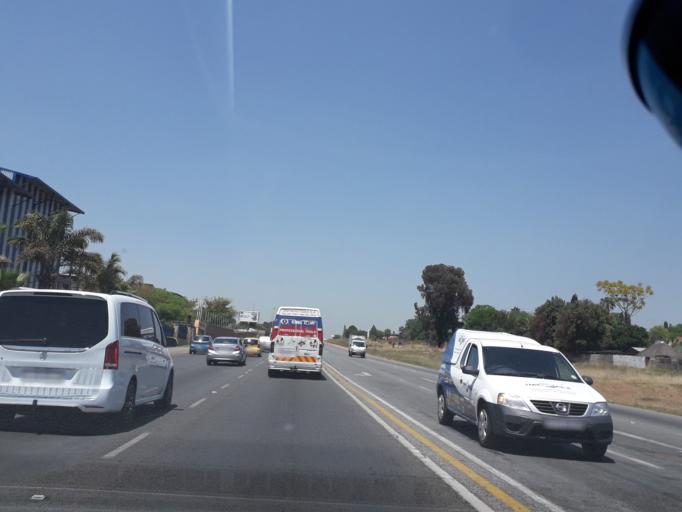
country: ZA
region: Gauteng
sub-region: City of Tshwane Metropolitan Municipality
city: Centurion
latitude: -25.8974
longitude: 28.1595
